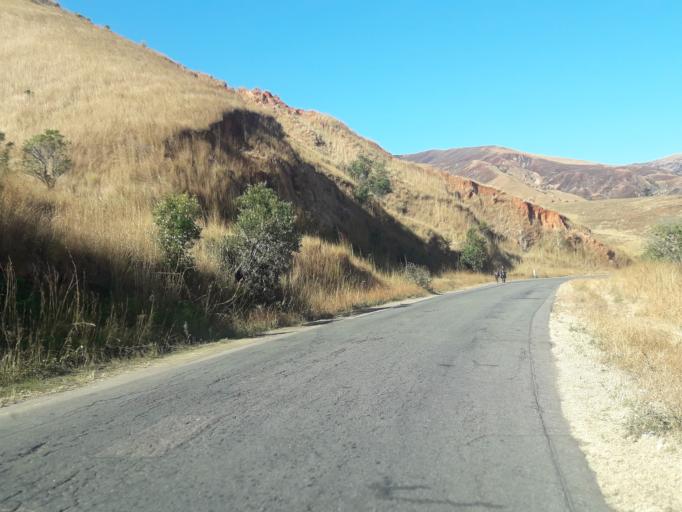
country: MG
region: Betsiboka
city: Maevatanana
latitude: -17.6237
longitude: 46.9505
